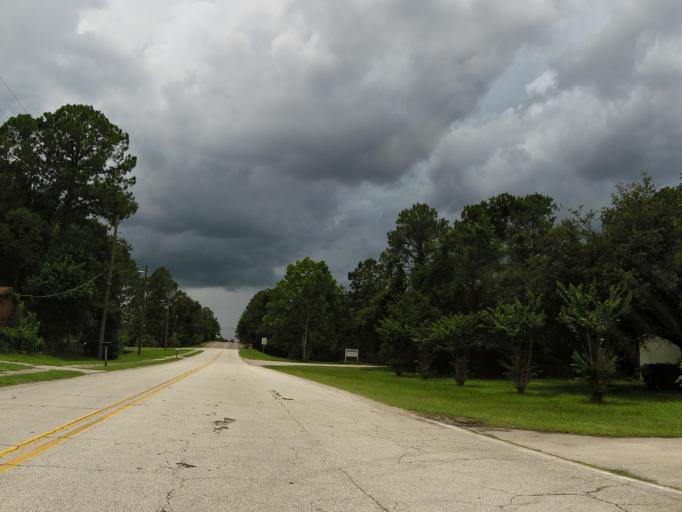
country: US
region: Florida
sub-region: Duval County
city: Jacksonville
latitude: 30.4141
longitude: -81.6540
